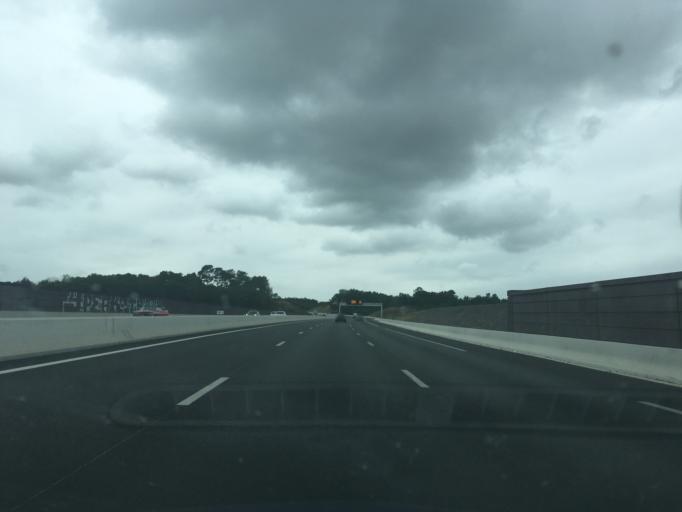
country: FR
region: Aquitaine
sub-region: Departement des Landes
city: Labenne
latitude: 43.5783
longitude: -1.4245
